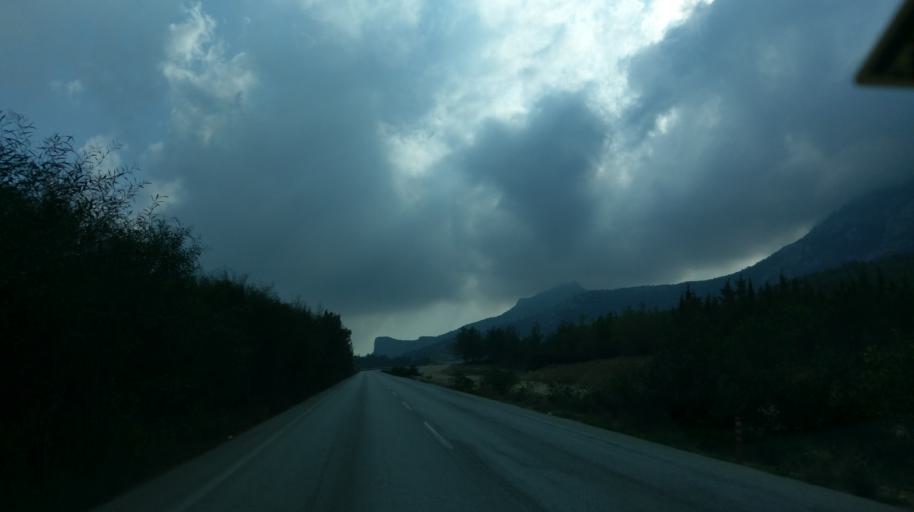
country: CY
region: Keryneia
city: Kyrenia
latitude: 35.3035
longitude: 33.4273
